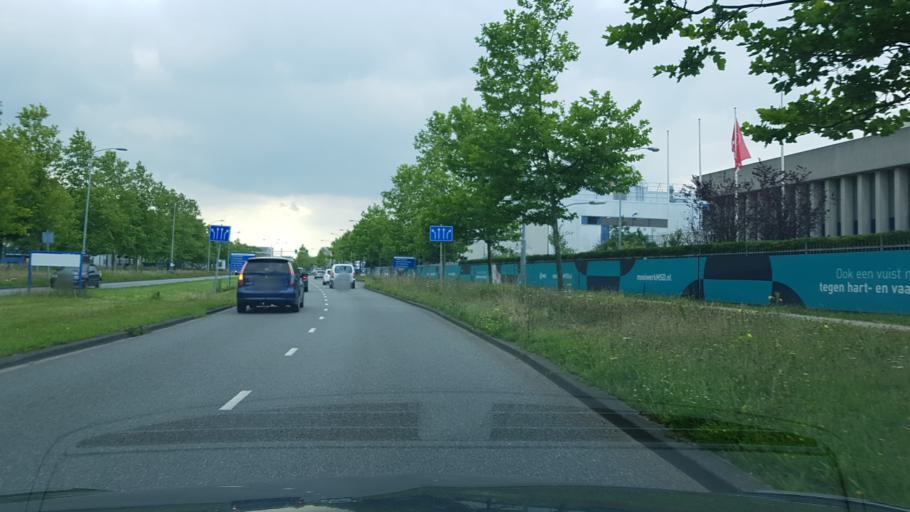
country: NL
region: North Holland
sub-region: Gemeente Haarlem
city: Haarlem
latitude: 52.3922
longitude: 4.6614
